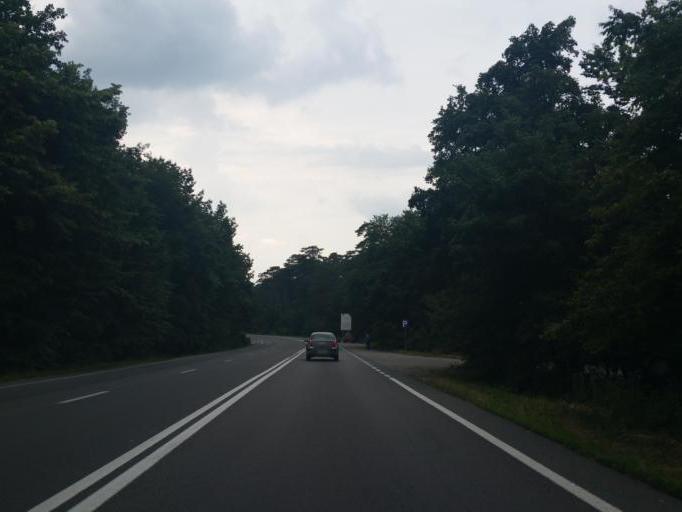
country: RO
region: Salaj
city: Zalau
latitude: 47.1666
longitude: 23.0811
